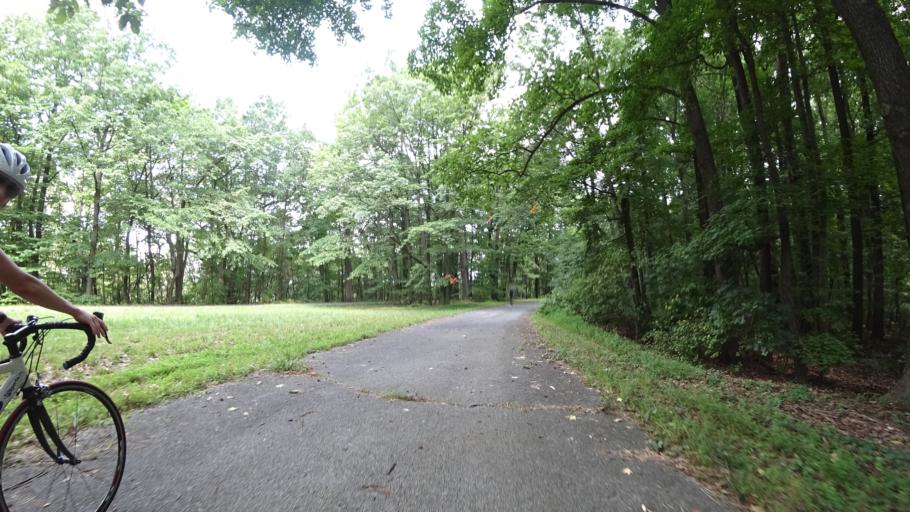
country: US
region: Maryland
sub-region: Prince George's County
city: Mount Rainier
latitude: 38.9087
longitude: -76.9753
